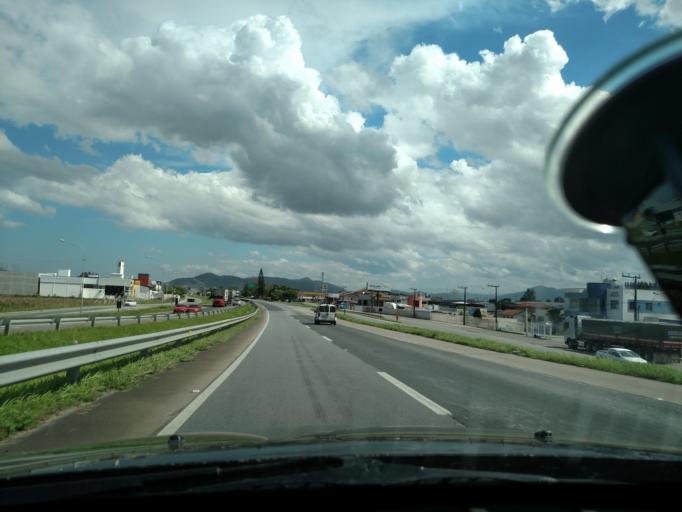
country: BR
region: Santa Catarina
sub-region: Tijucas
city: Tijucas
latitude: -27.2305
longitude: -48.6295
